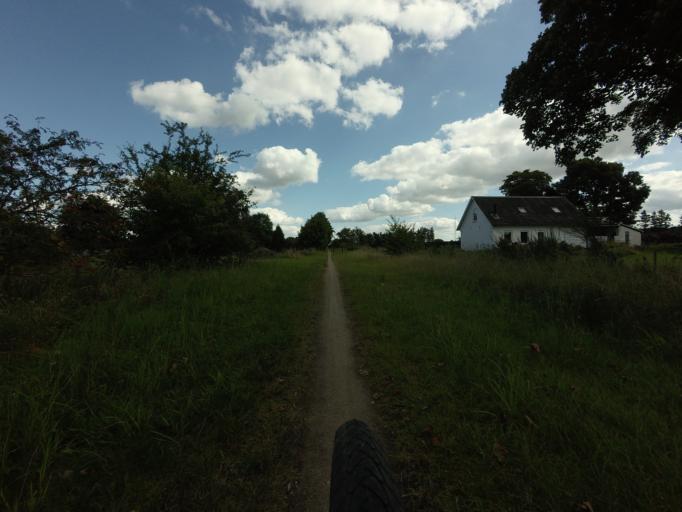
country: DK
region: Central Jutland
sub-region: Ikast-Brande Kommune
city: Brande
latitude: 55.9774
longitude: 9.2390
